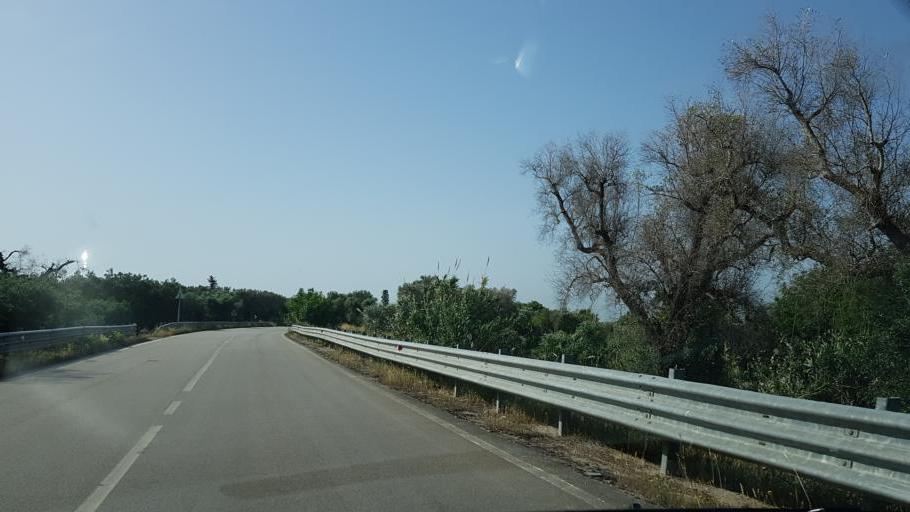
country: IT
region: Apulia
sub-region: Provincia di Brindisi
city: Mesagne
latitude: 40.4936
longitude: 17.8320
